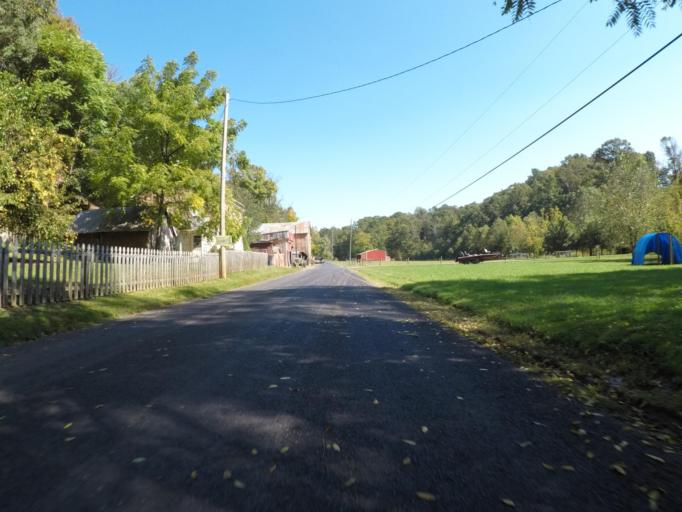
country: US
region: Maryland
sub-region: Carroll County
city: Hampstead
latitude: 39.5884
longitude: -76.8861
